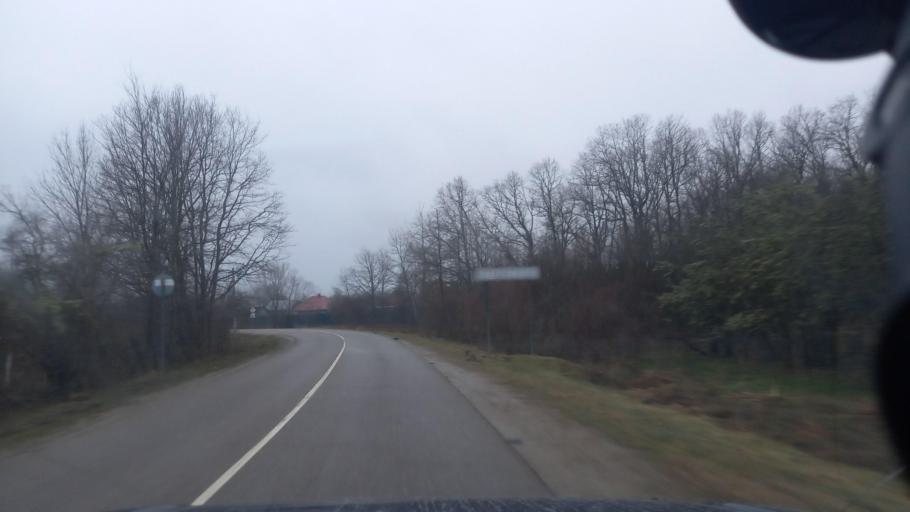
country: RU
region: Krasnodarskiy
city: Saratovskaya
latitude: 44.6496
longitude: 39.3196
